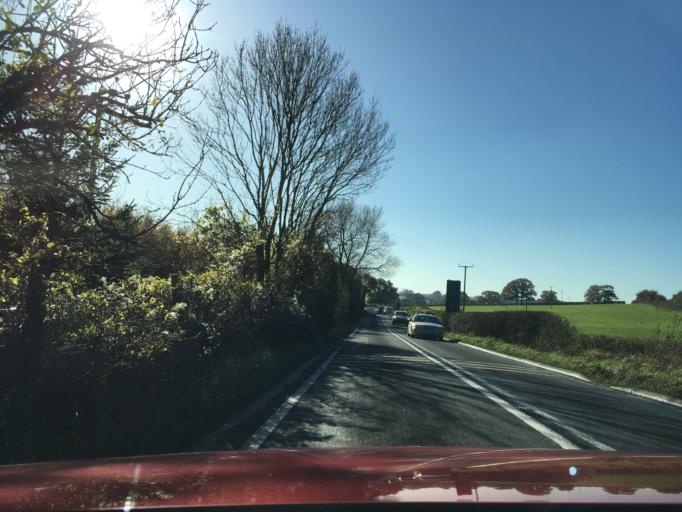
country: GB
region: England
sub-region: Somerset
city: Yeovil
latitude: 50.9109
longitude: -2.6241
